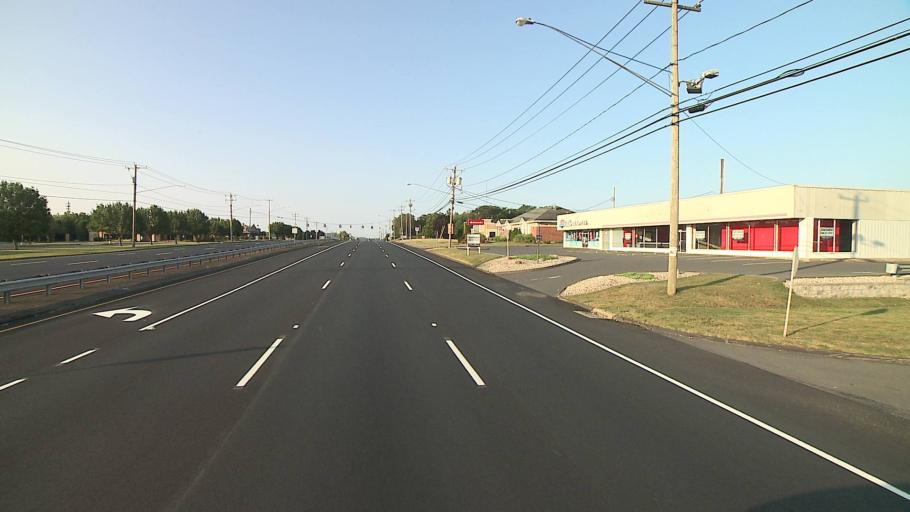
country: US
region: Connecticut
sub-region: Hartford County
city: Newington
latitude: 41.6609
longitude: -72.7228
